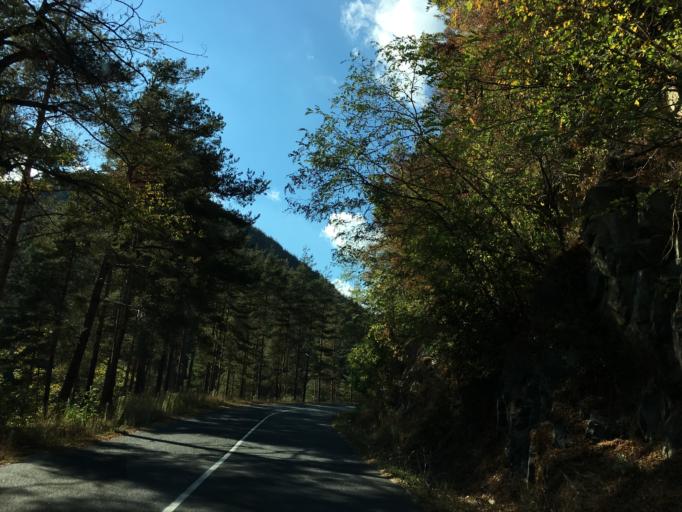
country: BG
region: Smolyan
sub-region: Obshtina Nedelino
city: Nedelino
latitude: 41.4362
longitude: 25.0246
